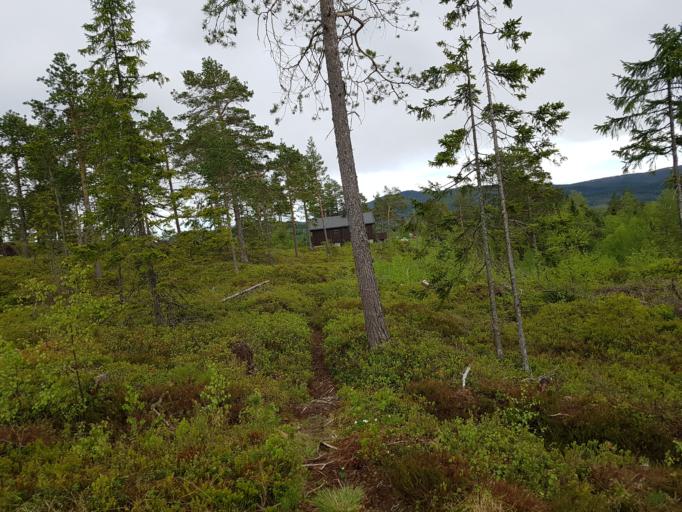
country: NO
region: Nord-Trondelag
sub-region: Levanger
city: Skogn
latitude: 63.6331
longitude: 11.2514
